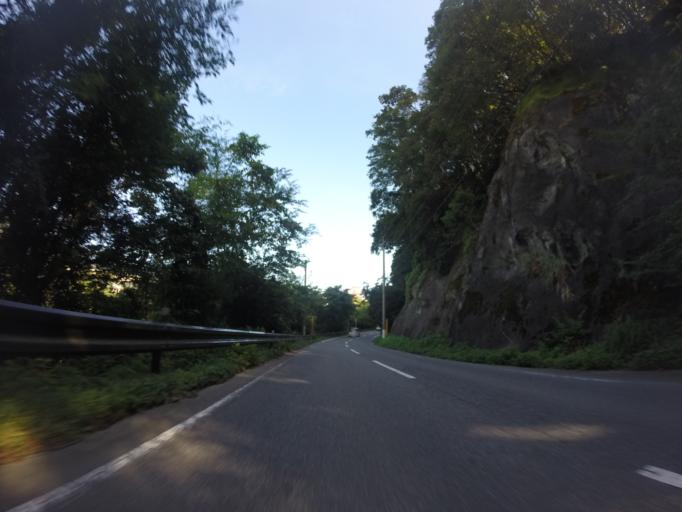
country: JP
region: Shizuoka
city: Fujinomiya
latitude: 35.3116
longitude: 138.4551
